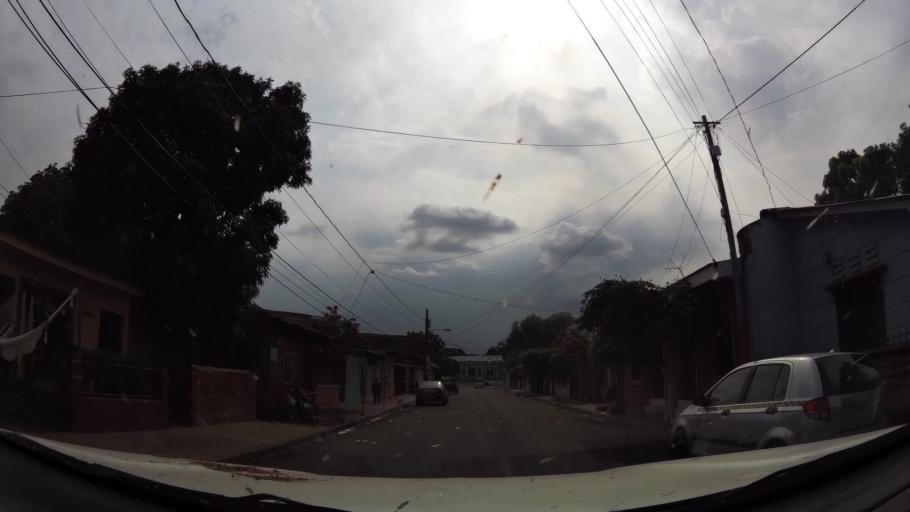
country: NI
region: Masaya
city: Masaya
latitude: 11.9739
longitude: -86.1022
